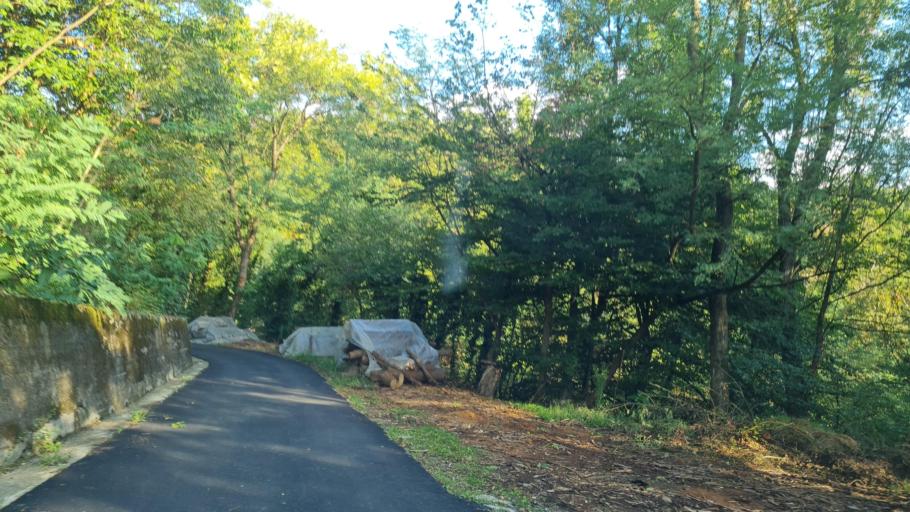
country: IT
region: Piedmont
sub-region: Provincia di Biella
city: Quaregna
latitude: 45.5875
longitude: 8.1634
